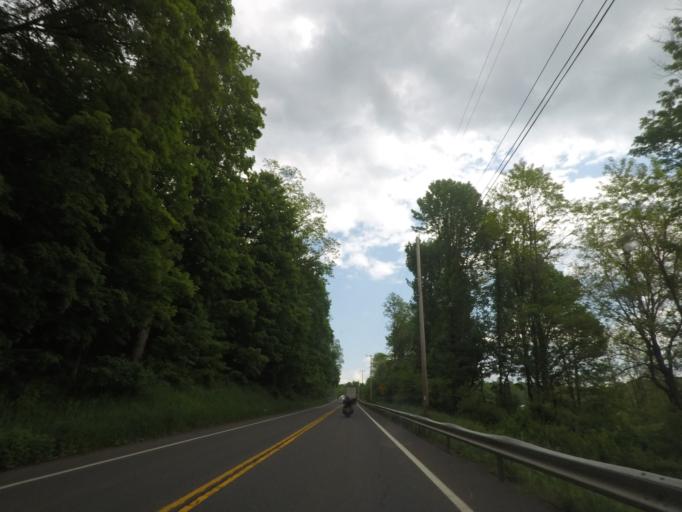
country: US
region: New York
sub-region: Dutchess County
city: Pine Plains
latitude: 42.0583
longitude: -73.6572
